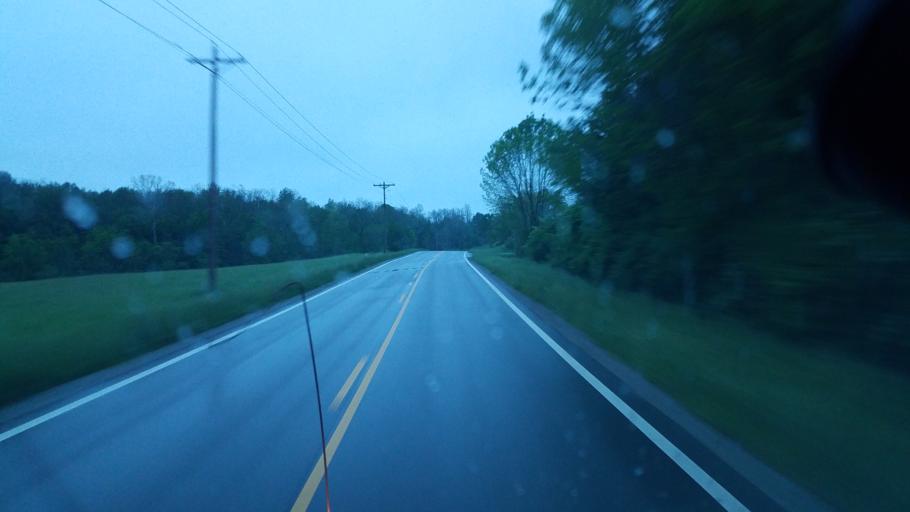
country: US
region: Ohio
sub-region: Highland County
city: Hillsboro
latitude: 39.2458
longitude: -83.5628
